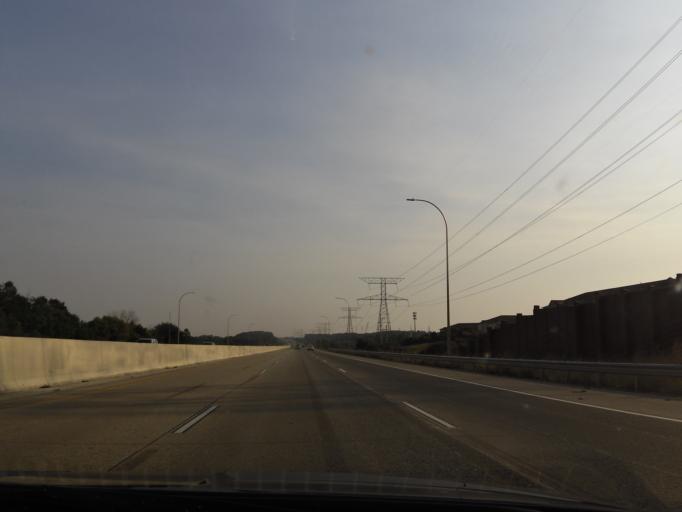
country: US
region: Minnesota
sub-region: Hennepin County
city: Maple Grove
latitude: 45.0518
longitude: -93.4522
